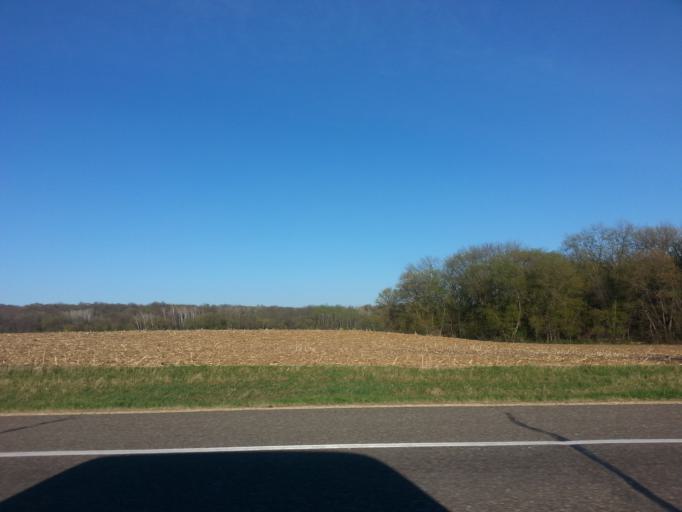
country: US
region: Minnesota
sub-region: Dakota County
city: Lakeville
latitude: 44.5601
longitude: -93.2076
